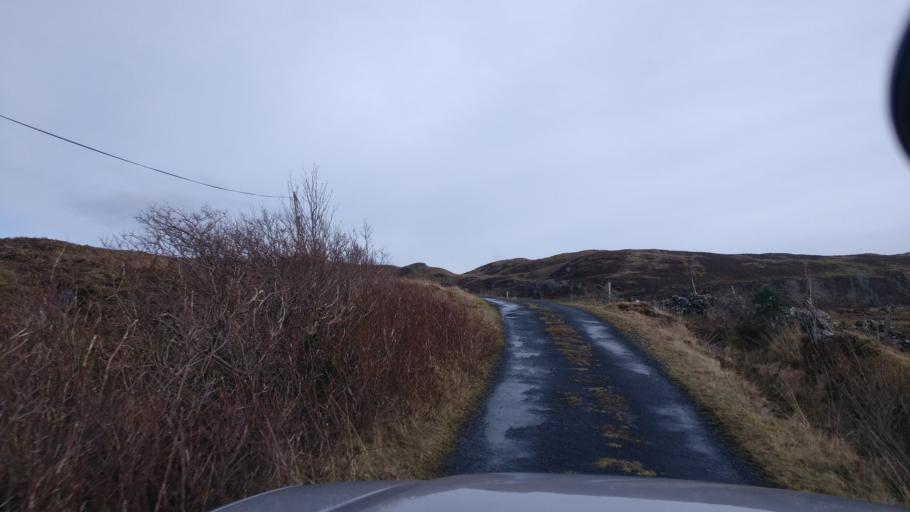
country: IE
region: Connaught
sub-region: County Galway
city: Oughterard
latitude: 53.5513
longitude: -9.4376
